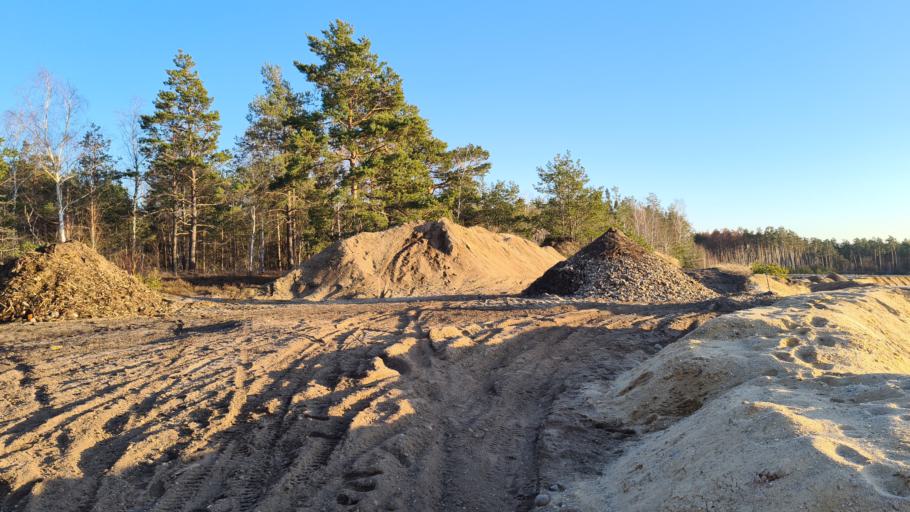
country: DE
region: Brandenburg
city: Finsterwalde
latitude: 51.6371
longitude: 13.6593
